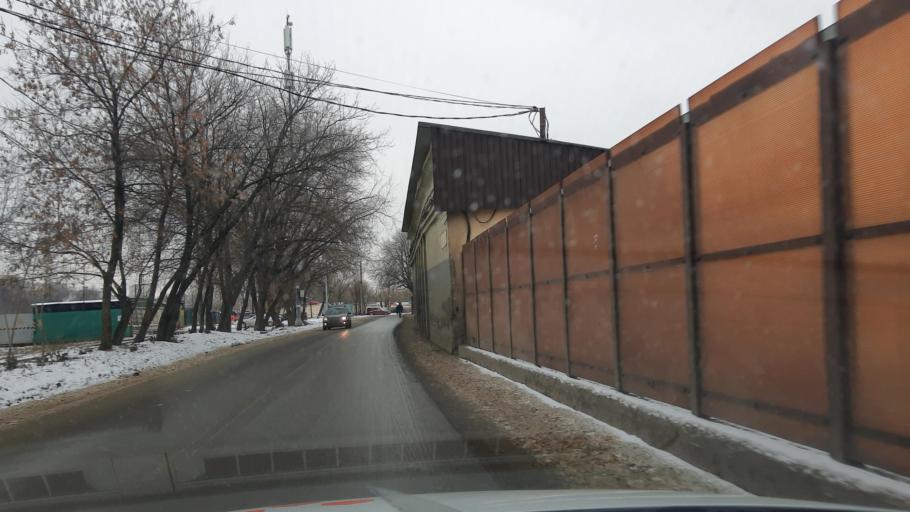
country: RU
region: Moscow
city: Lyublino
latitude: 55.6739
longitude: 37.7357
